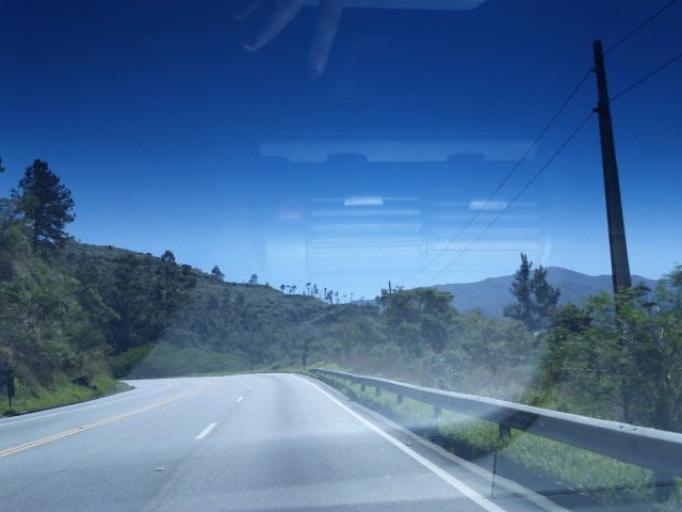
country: BR
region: Sao Paulo
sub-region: Campos Do Jordao
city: Campos do Jordao
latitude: -22.8476
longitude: -45.6145
